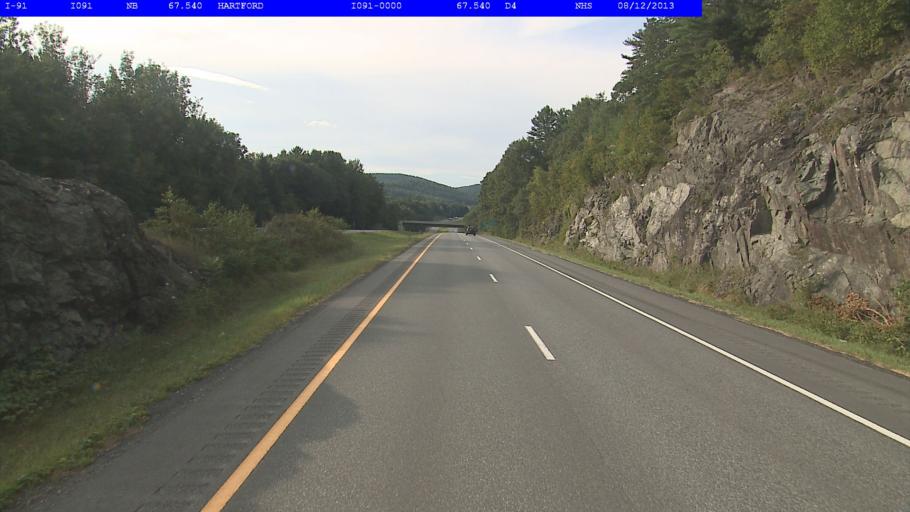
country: US
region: Vermont
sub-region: Windsor County
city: White River Junction
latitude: 43.6088
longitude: -72.3429
